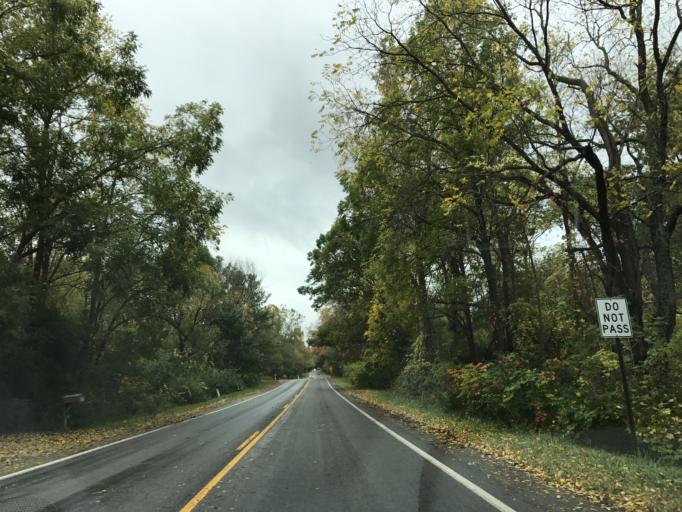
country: US
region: Michigan
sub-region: Washtenaw County
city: Ann Arbor
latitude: 42.3201
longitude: -83.6615
